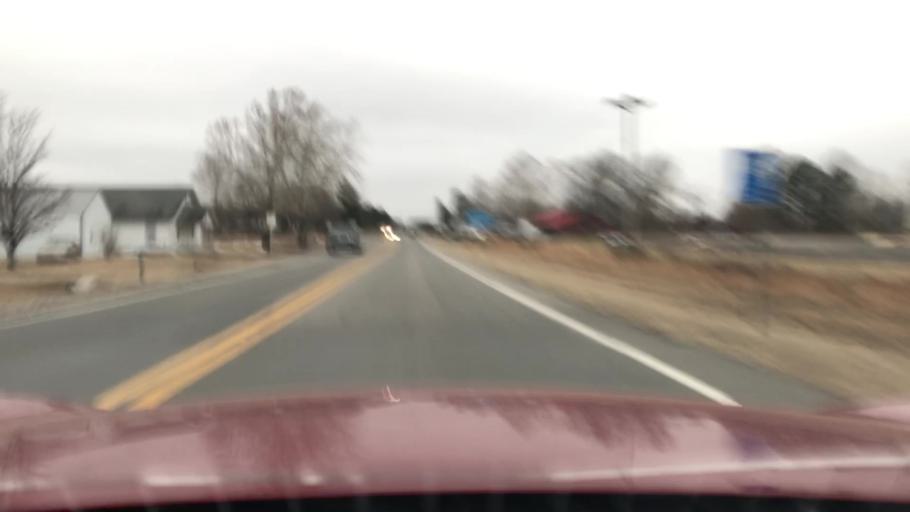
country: US
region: Oklahoma
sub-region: Sequoyah County
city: Sallisaw
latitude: 35.5084
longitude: -94.7722
